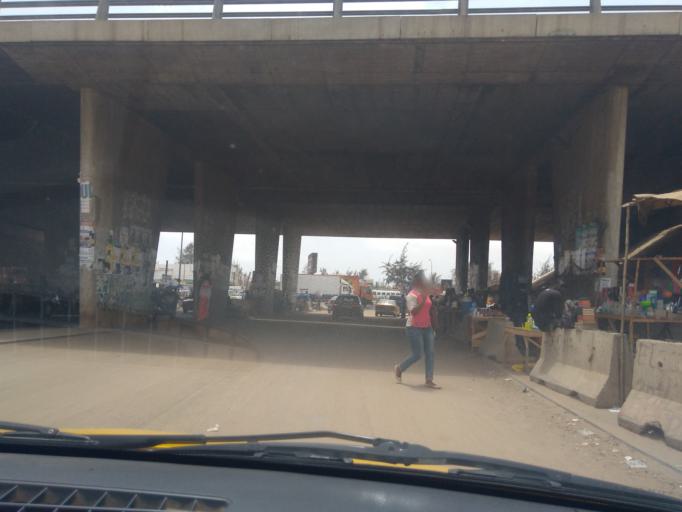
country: SN
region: Dakar
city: Pikine
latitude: 14.7444
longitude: -17.4243
